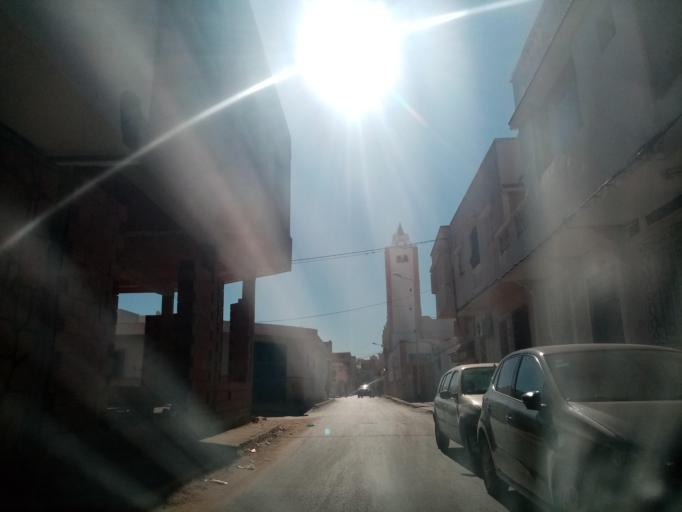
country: TN
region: Qabis
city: Gabes
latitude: 33.8803
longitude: 10.0894
